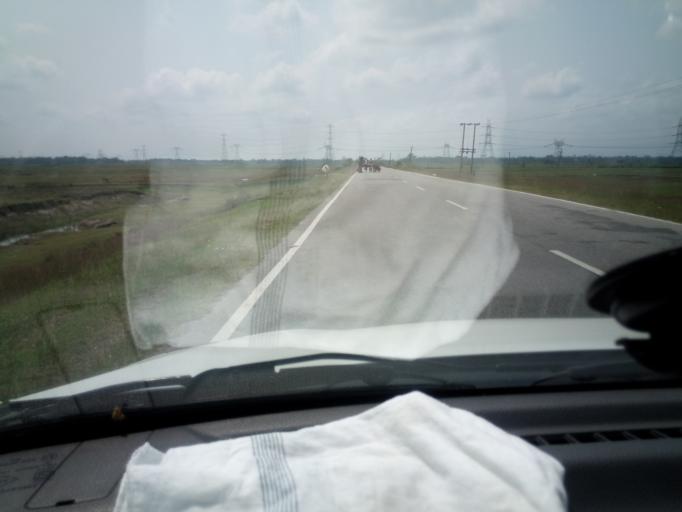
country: IN
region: Assam
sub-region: Udalguri
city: Udalguri
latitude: 26.7288
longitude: 92.1775
